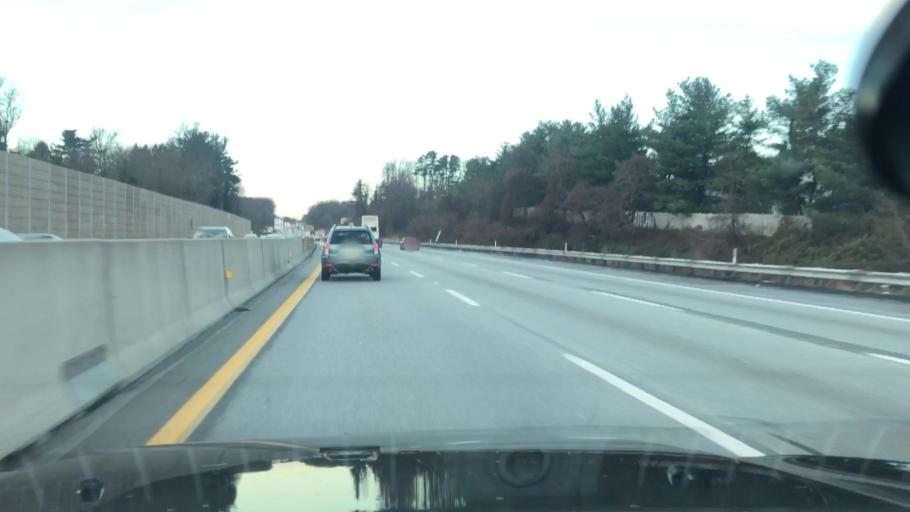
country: US
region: Pennsylvania
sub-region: Bucks County
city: Feasterville
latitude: 40.1443
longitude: -75.0070
